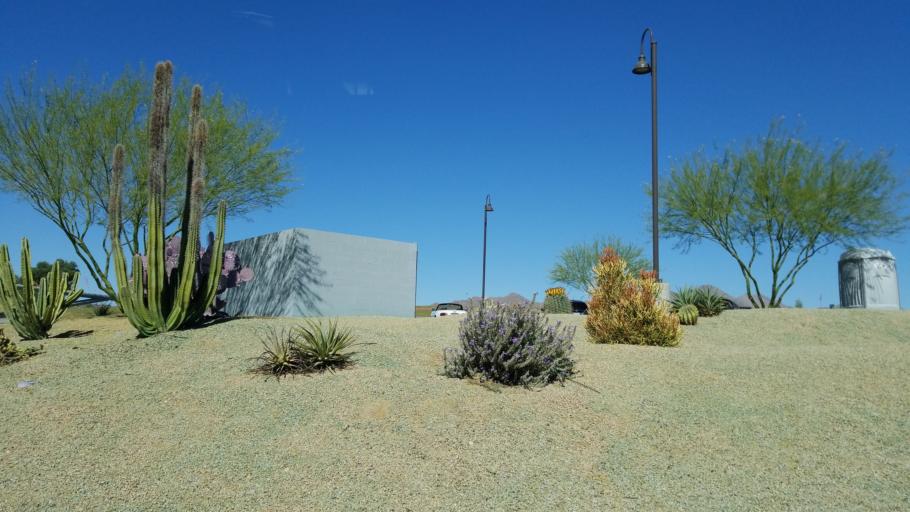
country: US
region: Arizona
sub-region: Maricopa County
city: Fountain Hills
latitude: 33.6021
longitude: -111.7088
